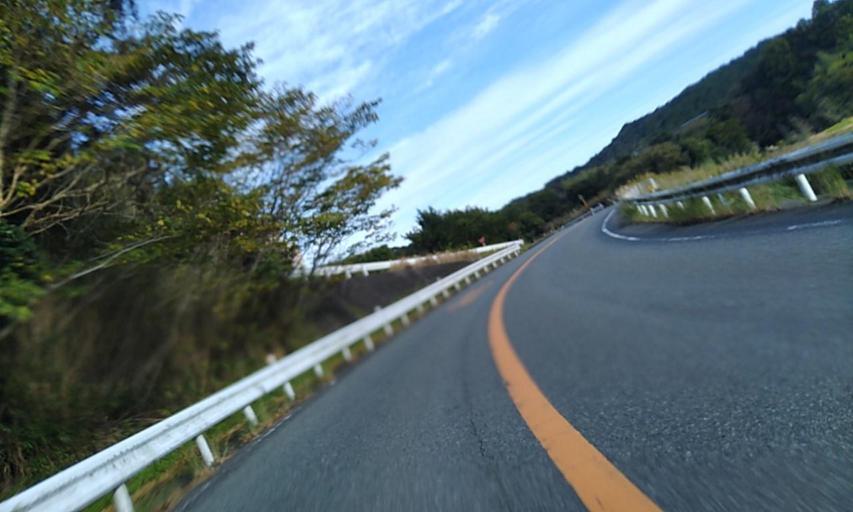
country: JP
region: Mie
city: Ise
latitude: 34.3575
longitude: 136.7650
